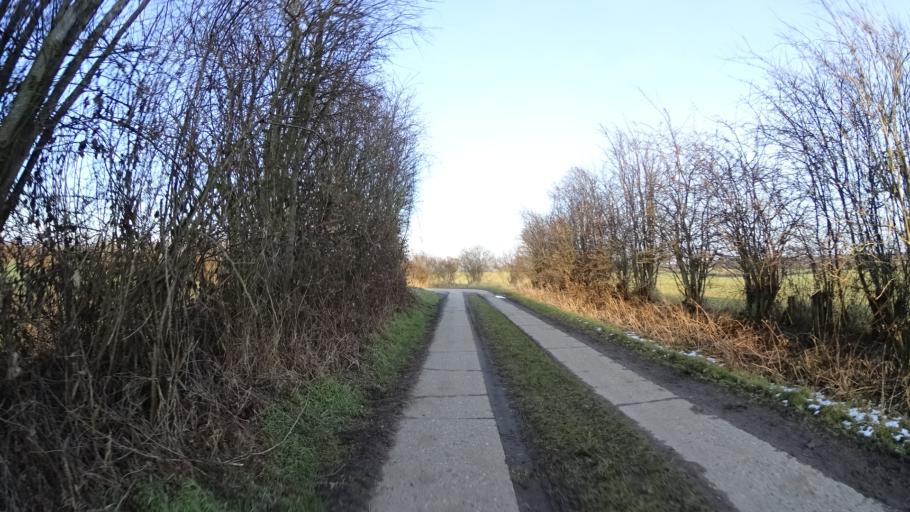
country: DE
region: Schleswig-Holstein
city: Stakendorf
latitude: 54.3756
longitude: 10.4252
